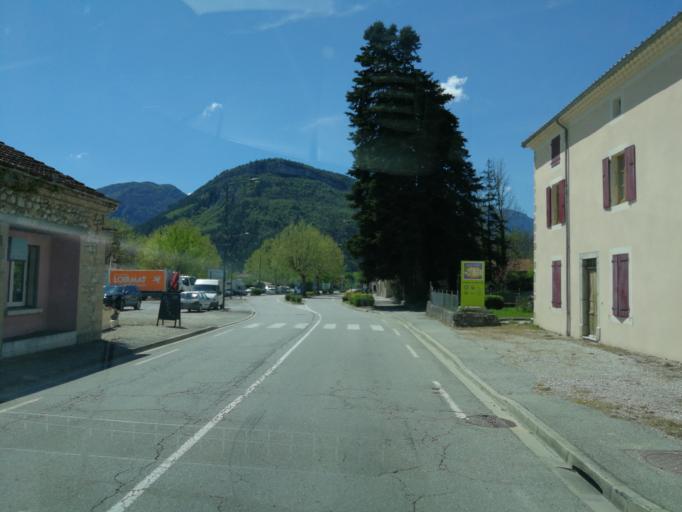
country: FR
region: Rhone-Alpes
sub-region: Departement de la Drome
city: Die
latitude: 44.7059
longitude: 5.2595
